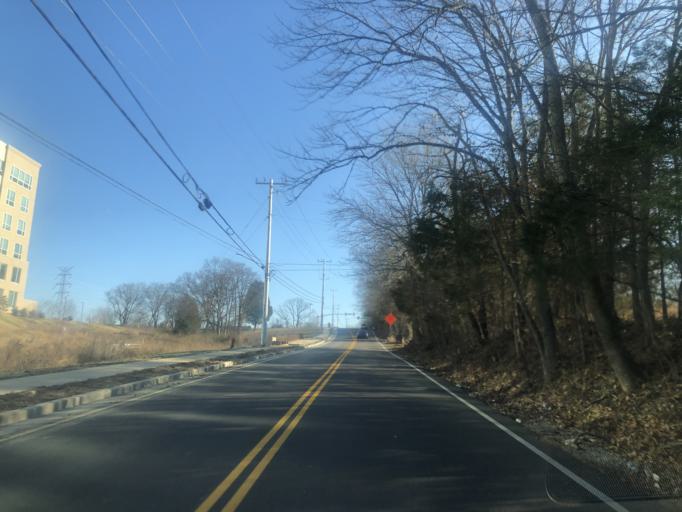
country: US
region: Tennessee
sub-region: Rutherford County
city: La Vergne
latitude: 36.0293
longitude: -86.6467
